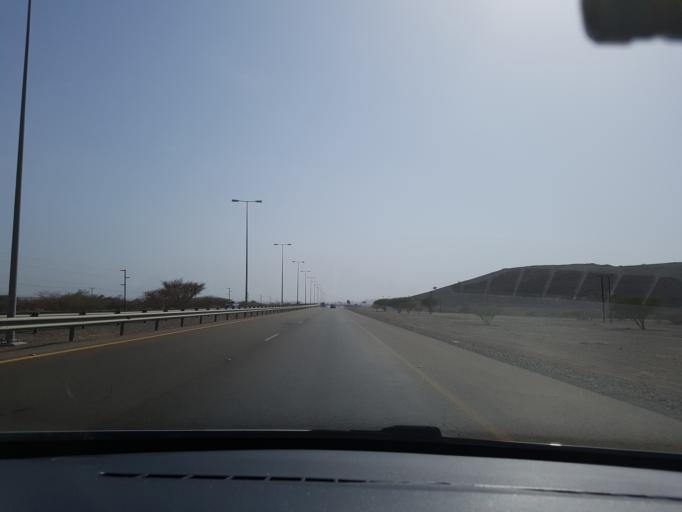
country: OM
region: Al Batinah
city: Al Liwa'
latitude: 24.3992
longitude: 56.5779
